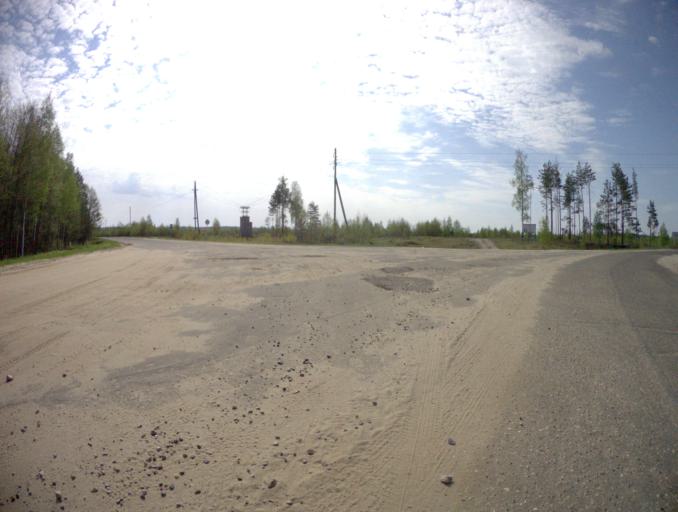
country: RU
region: Ivanovo
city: Yuzha
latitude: 56.5222
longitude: 42.0495
